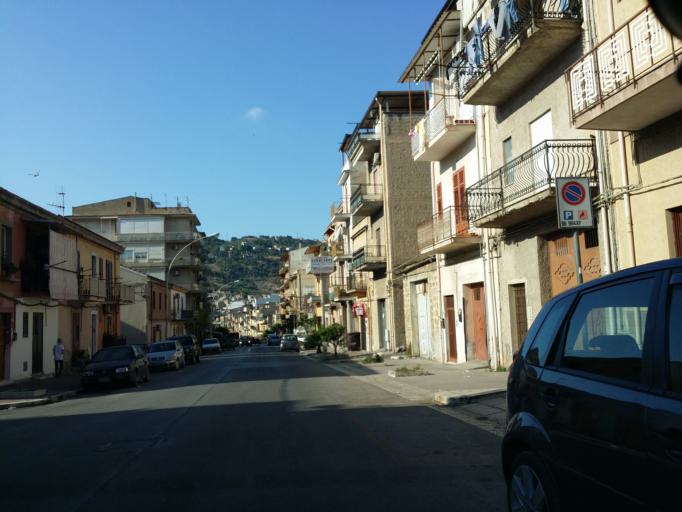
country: IT
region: Sicily
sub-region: Palermo
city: Misilmeri
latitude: 38.0270
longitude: 13.4479
